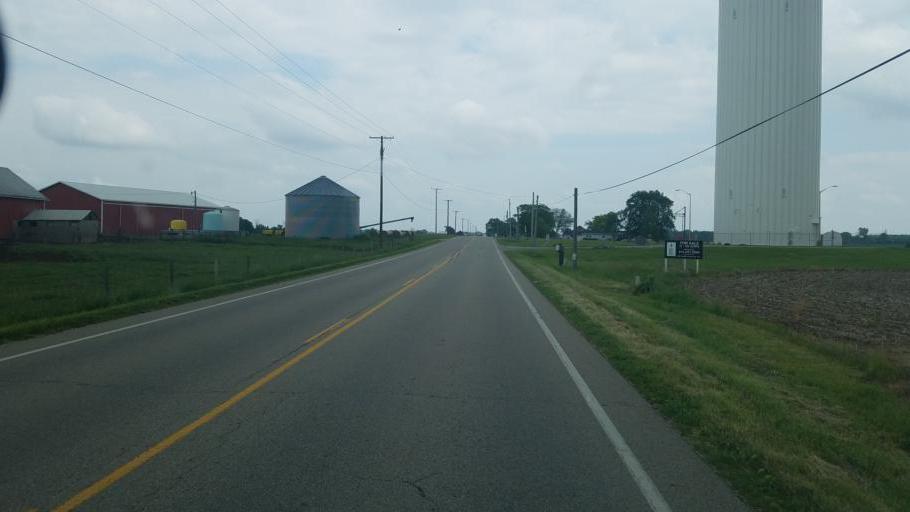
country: US
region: Ohio
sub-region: Union County
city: New California
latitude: 40.1885
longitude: -83.2858
